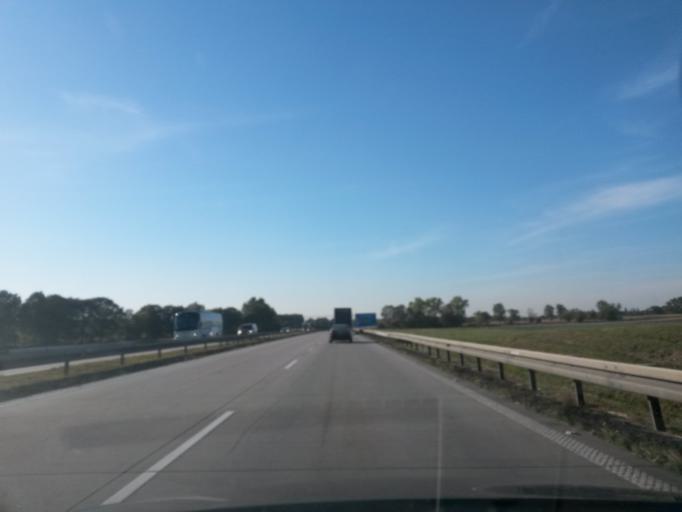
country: PL
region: Lower Silesian Voivodeship
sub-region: Powiat sredzki
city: Udanin
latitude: 51.0811
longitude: 16.4329
